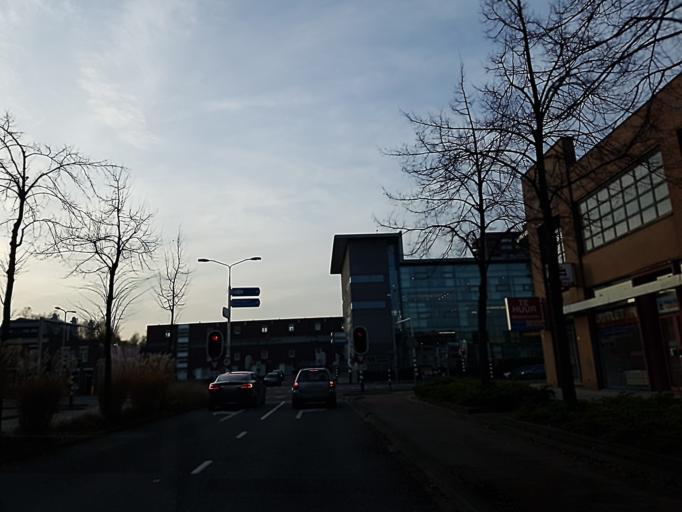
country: NL
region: North Brabant
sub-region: Roosendaal
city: Roosendaal
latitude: 51.5295
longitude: 4.4540
